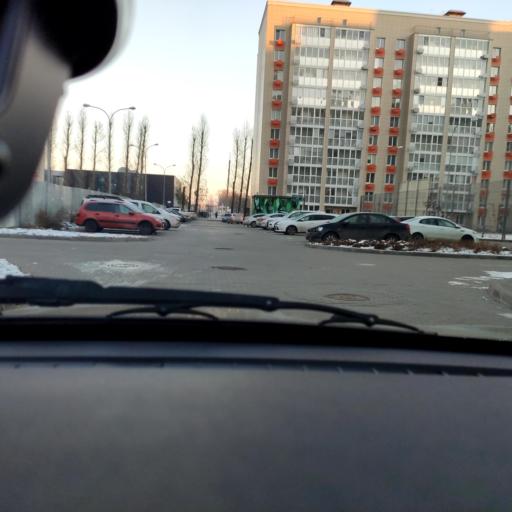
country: RU
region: Samara
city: Tol'yatti
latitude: 53.5481
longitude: 49.3124
